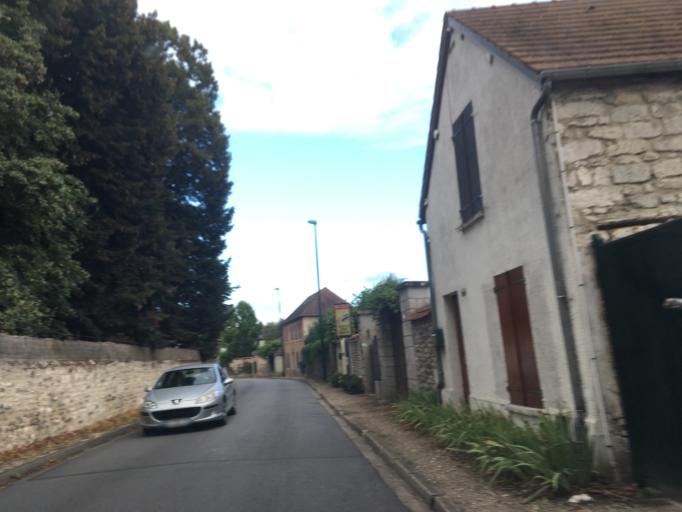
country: FR
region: Haute-Normandie
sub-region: Departement de l'Eure
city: Saint-Just
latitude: 49.1310
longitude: 1.4471
